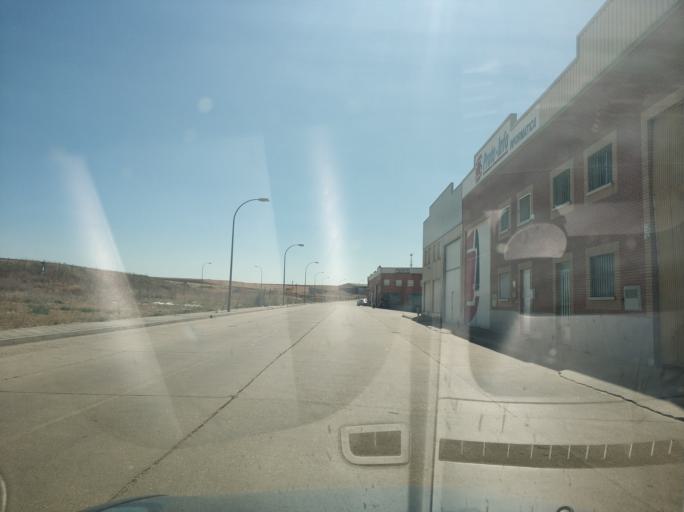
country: ES
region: Castille and Leon
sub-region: Provincia de Salamanca
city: Villares de la Reina
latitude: 40.9915
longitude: -5.6342
